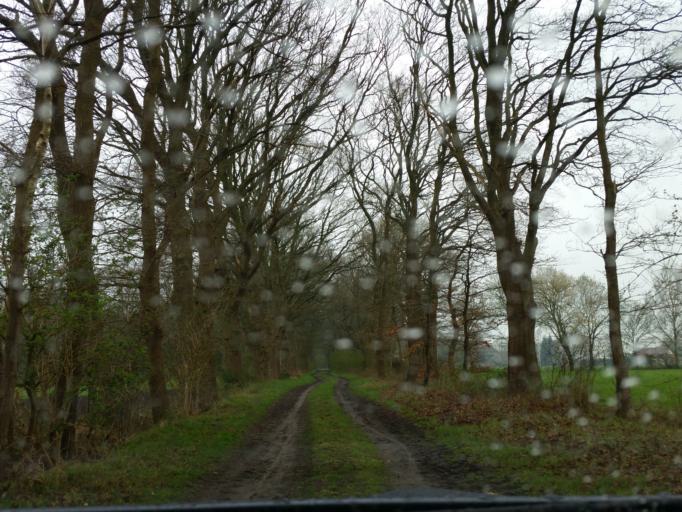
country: DE
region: Lower Saxony
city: Hipstedt
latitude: 53.4870
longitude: 8.9595
